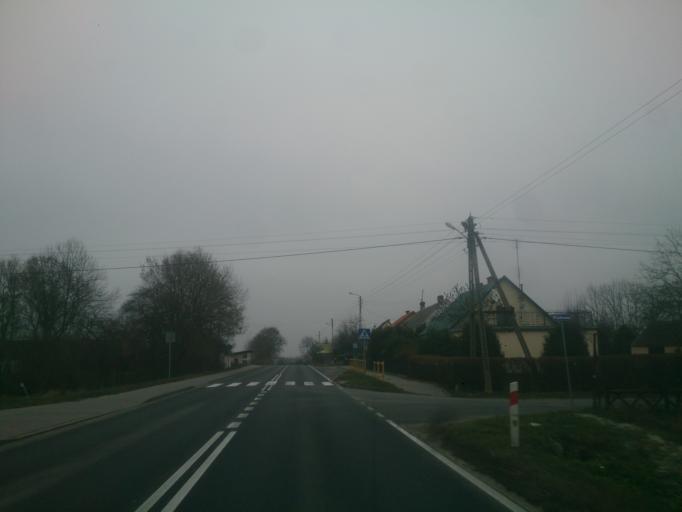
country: PL
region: Warmian-Masurian Voivodeship
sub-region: Powiat nowomiejski
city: Kurzetnik
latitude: 53.3901
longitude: 19.5725
